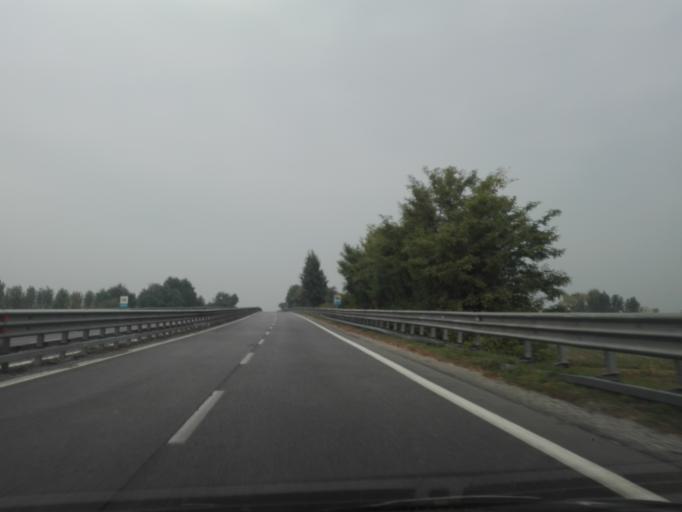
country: IT
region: Veneto
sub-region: Provincia di Verona
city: Legnago
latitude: 45.1736
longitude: 11.2887
